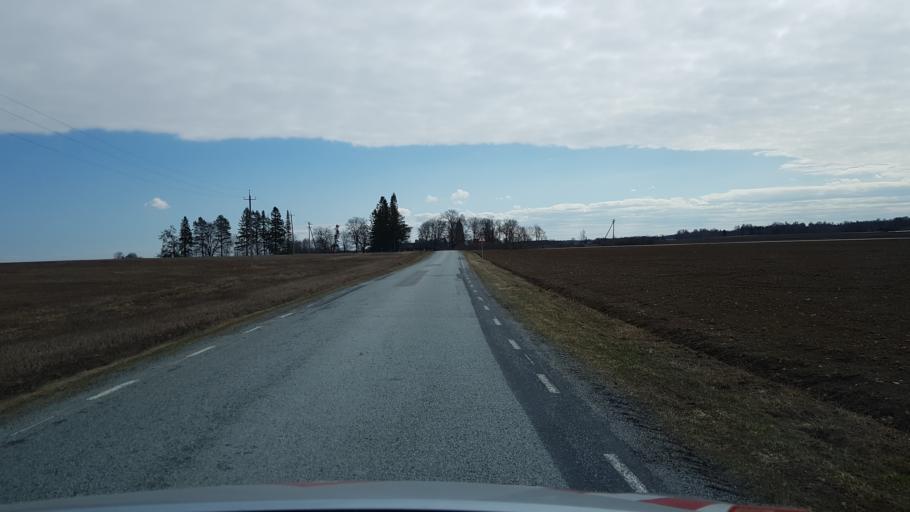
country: EE
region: Laeaene-Virumaa
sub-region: Haljala vald
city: Haljala
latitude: 59.4256
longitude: 26.2227
